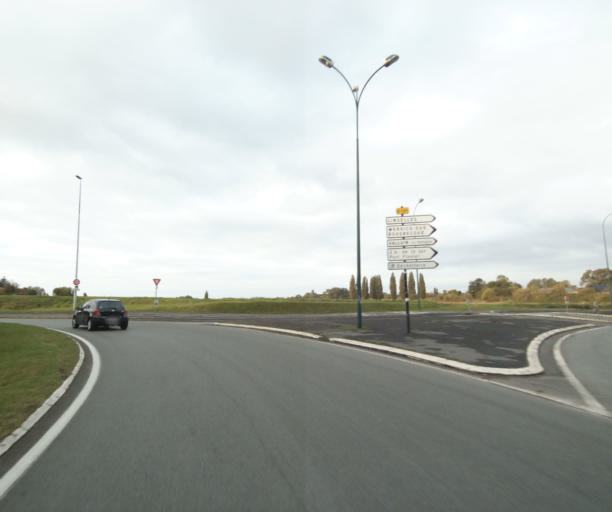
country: FR
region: Nord-Pas-de-Calais
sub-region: Departement du Nord
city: Roncq
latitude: 50.7658
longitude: 3.1206
